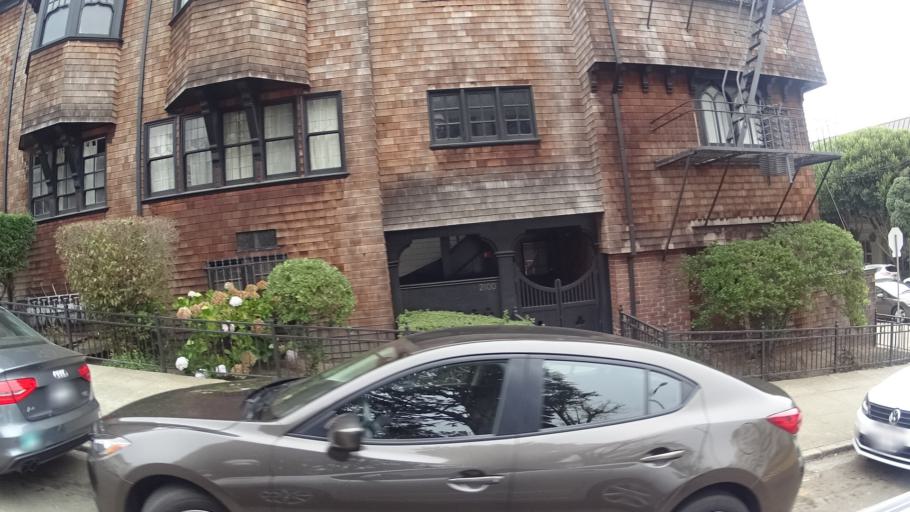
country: US
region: California
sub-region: San Francisco County
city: San Francisco
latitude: 37.7903
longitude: -122.4459
